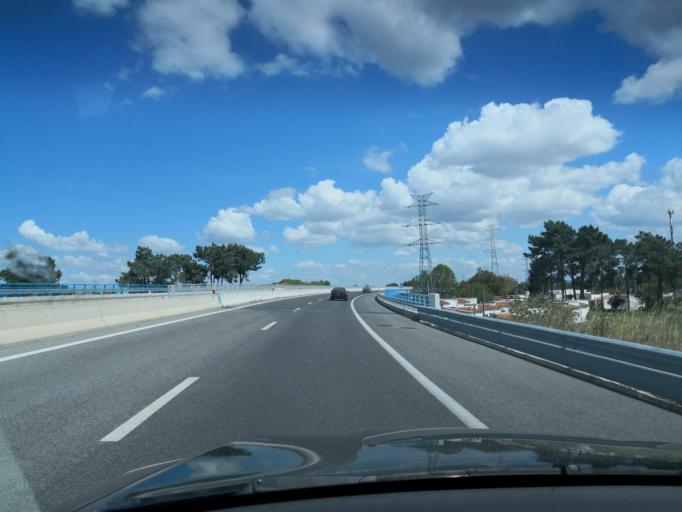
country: PT
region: Setubal
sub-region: Seixal
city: Amora
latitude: 38.6061
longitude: -9.1392
